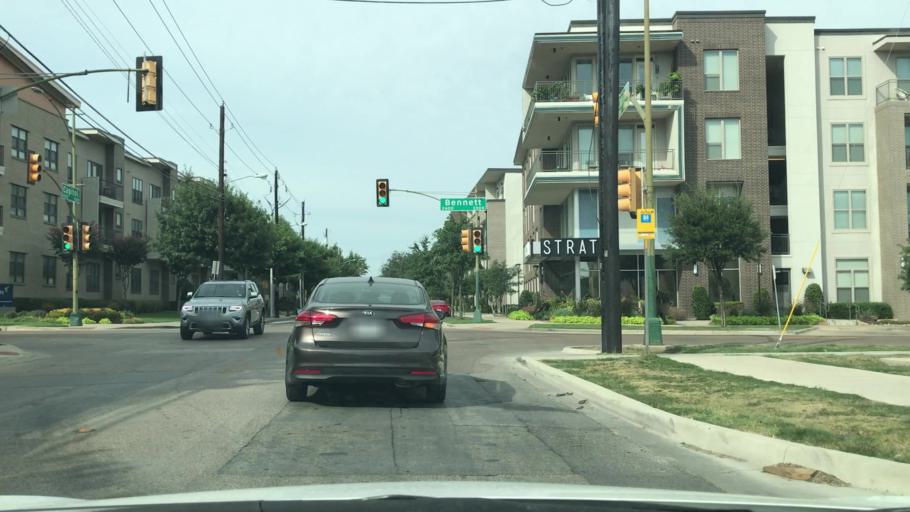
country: US
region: Texas
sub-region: Dallas County
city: Highland Park
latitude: 32.8119
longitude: -96.7813
